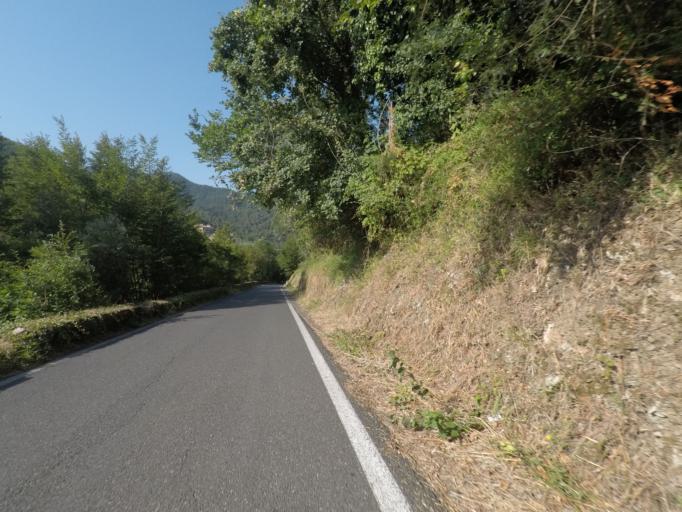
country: IT
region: Liguria
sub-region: Provincia di La Spezia
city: Casano-Dogana-Isola
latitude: 44.0918
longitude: 10.0495
